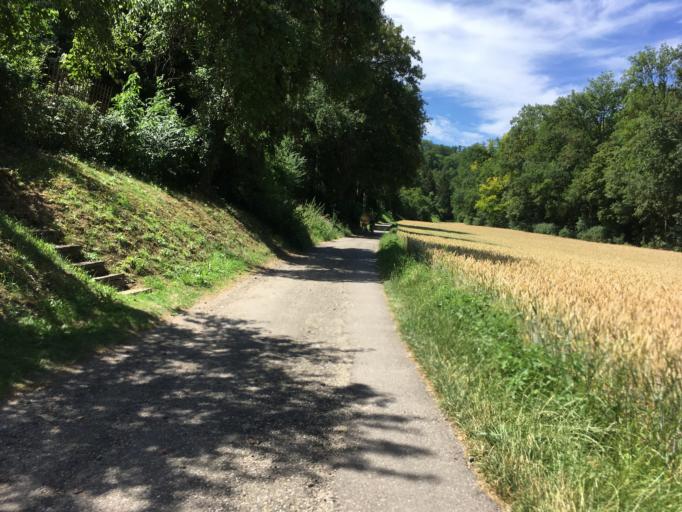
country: DE
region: Baden-Wuerttemberg
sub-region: Regierungsbezirk Stuttgart
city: Vaihingen an der Enz
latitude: 48.9156
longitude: 8.9677
